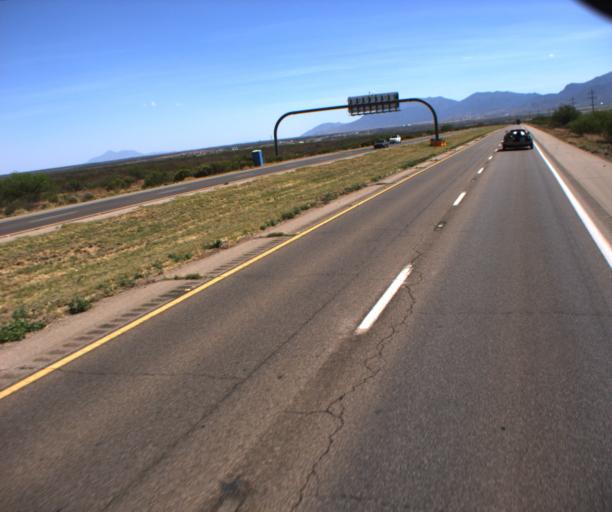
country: US
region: Arizona
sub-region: Cochise County
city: Huachuca City
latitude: 31.6714
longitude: -110.3504
